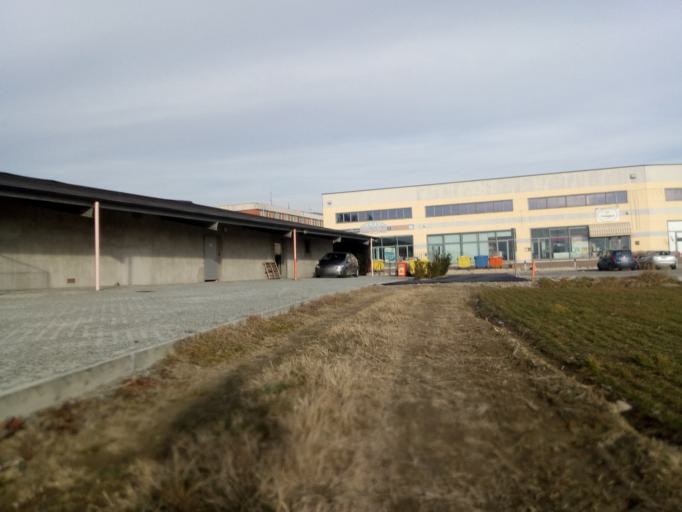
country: IT
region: Piedmont
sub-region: Provincia di Torino
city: Cascinette d'Ivrea
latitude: 45.4700
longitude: 7.9127
